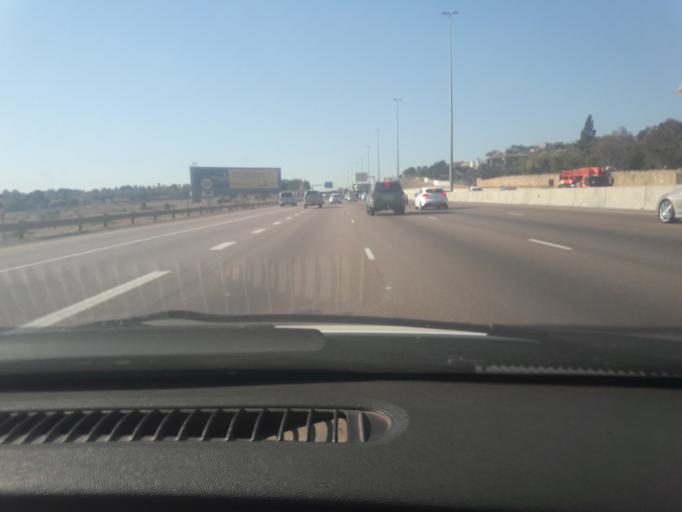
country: ZA
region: Gauteng
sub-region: City of Tshwane Metropolitan Municipality
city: Centurion
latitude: -25.8236
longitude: 28.2491
